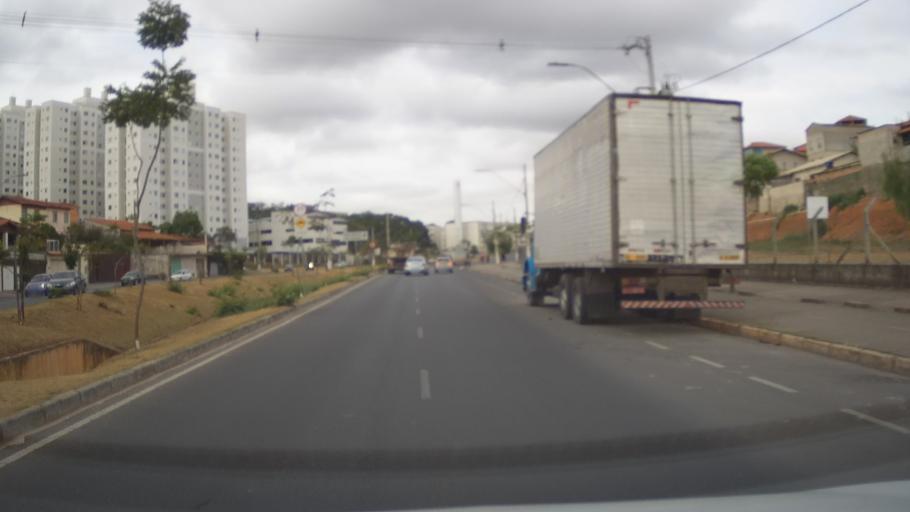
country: BR
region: Minas Gerais
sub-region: Belo Horizonte
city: Belo Horizonte
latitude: -19.8308
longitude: -43.9745
